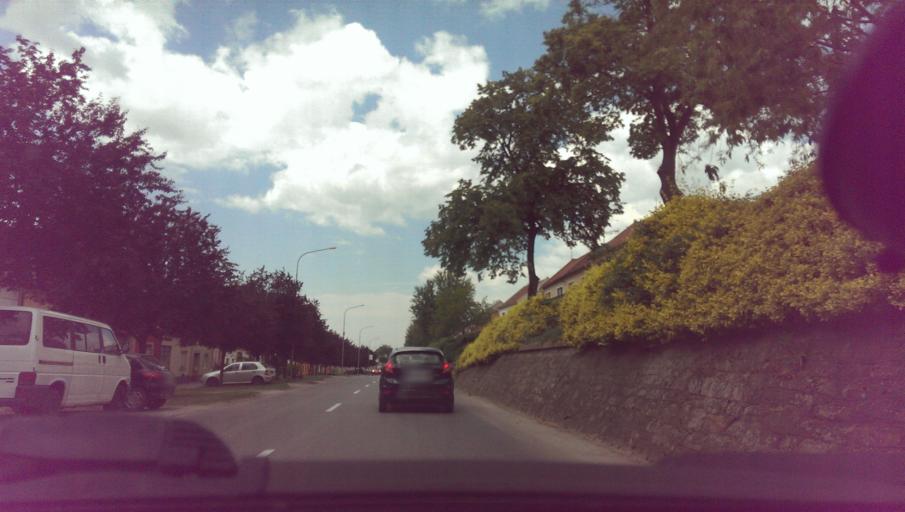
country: CZ
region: Zlin
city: Hluk
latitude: 48.9863
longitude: 17.5315
